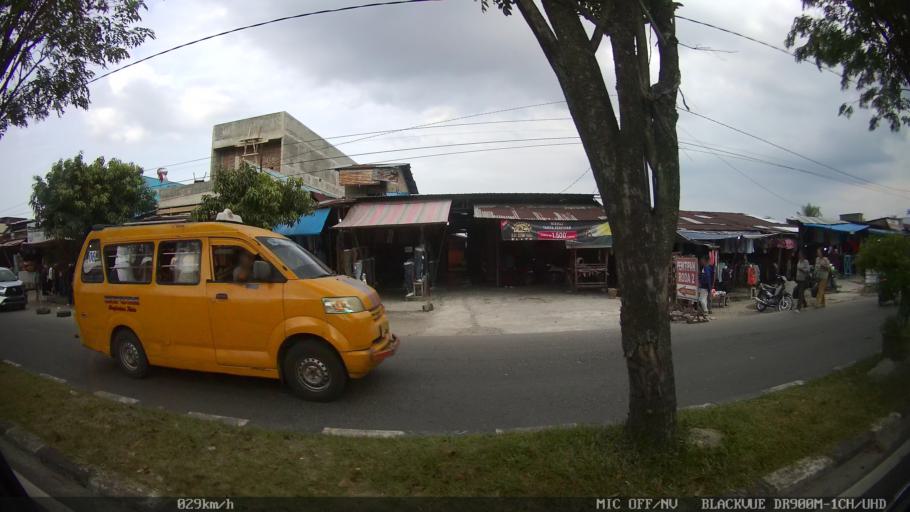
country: ID
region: North Sumatra
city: Sunggal
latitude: 3.5425
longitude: 98.6046
